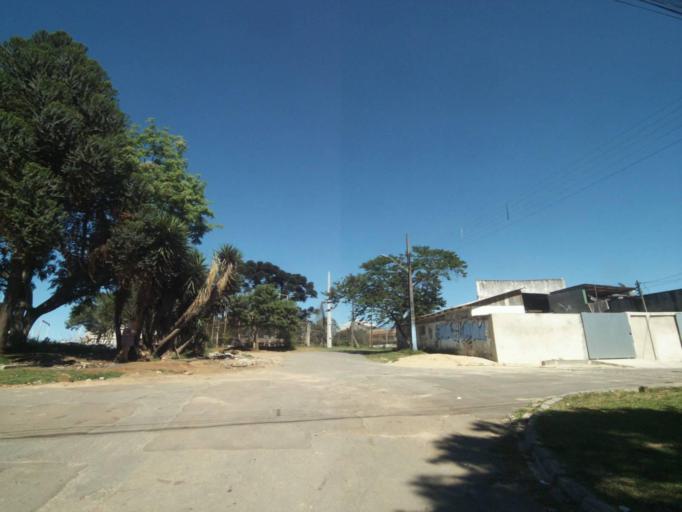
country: BR
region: Parana
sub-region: Curitiba
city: Curitiba
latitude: -25.4863
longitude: -49.3395
